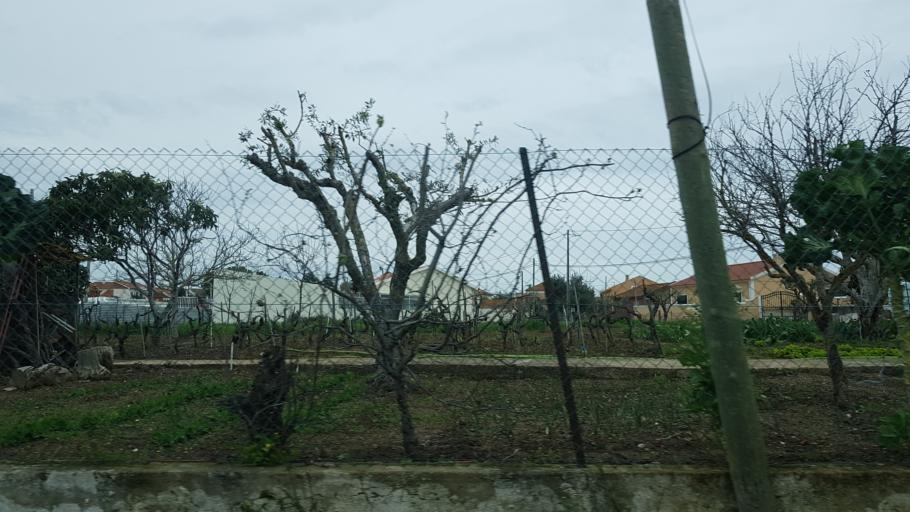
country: PT
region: Lisbon
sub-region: Alenquer
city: Carregado
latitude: 39.0401
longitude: -8.9786
